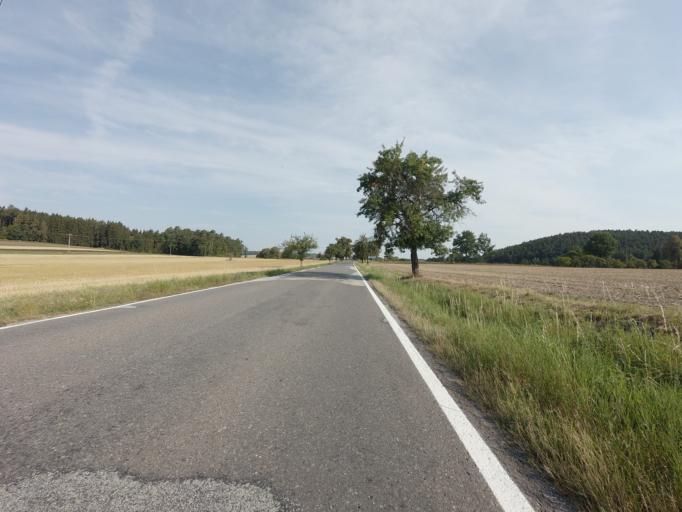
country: CZ
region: Jihocesky
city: Milevsko
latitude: 49.4658
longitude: 14.3619
